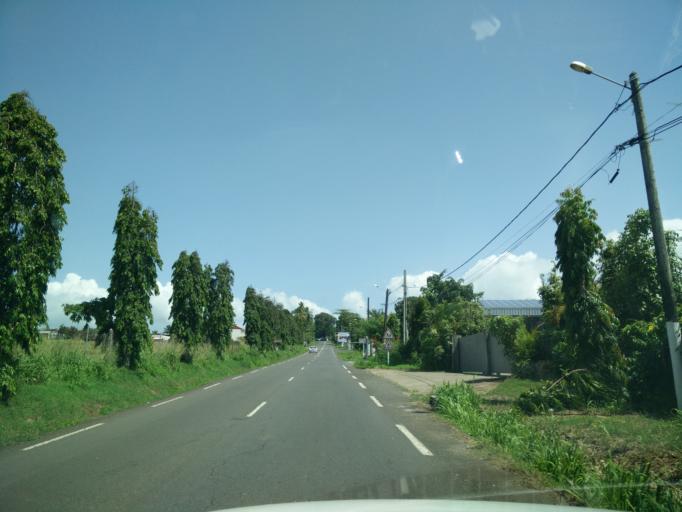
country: GP
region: Guadeloupe
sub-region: Guadeloupe
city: Petit-Bourg
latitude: 16.1811
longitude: -61.5878
